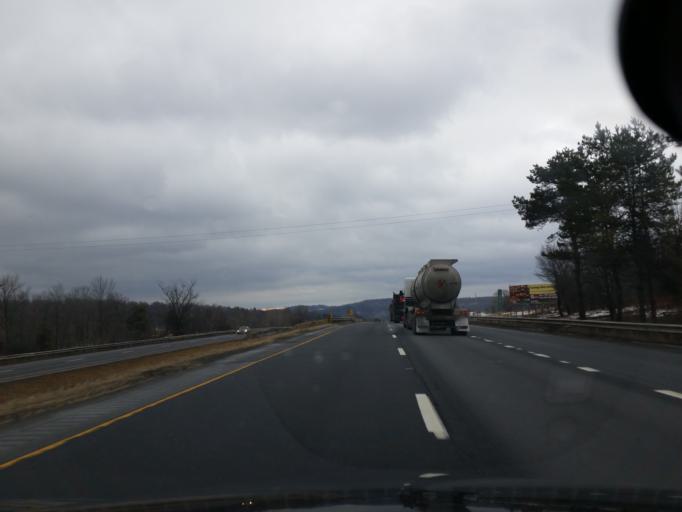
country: US
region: Pennsylvania
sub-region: Lackawanna County
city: Dalton
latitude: 41.6721
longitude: -75.6807
